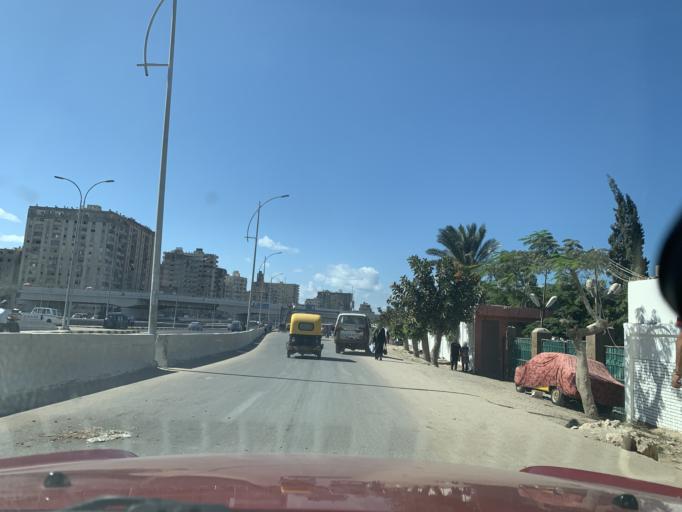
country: EG
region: Alexandria
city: Alexandria
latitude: 31.2185
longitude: 29.9959
